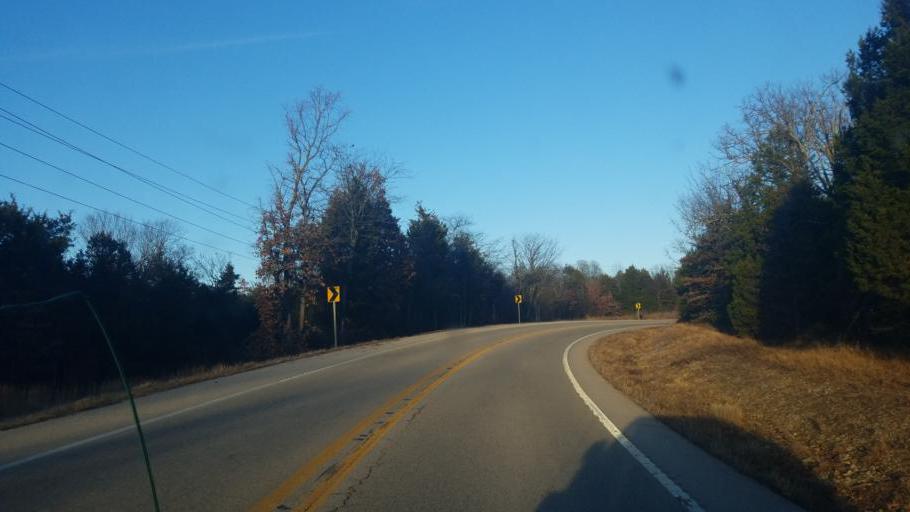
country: US
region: Arkansas
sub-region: Baxter County
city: Mountain Home
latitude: 36.3857
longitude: -92.1897
